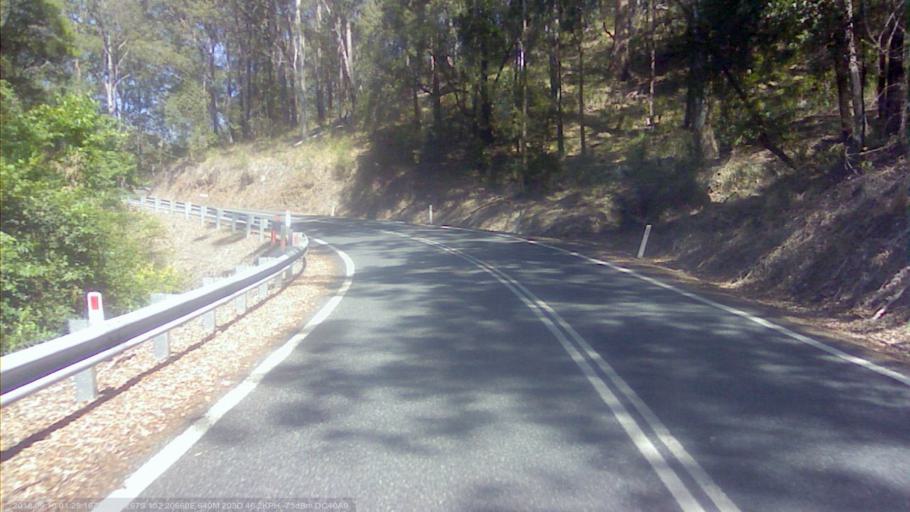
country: AU
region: New South Wales
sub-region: Port Macquarie-Hastings
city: Kendall
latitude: -31.4227
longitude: 152.2066
